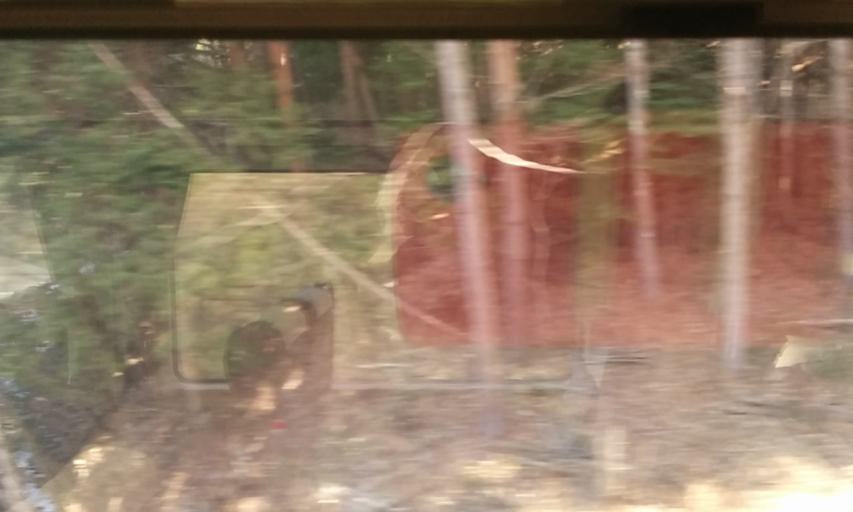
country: JP
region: Nagano
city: Tatsuno
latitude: 35.9744
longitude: 137.8234
